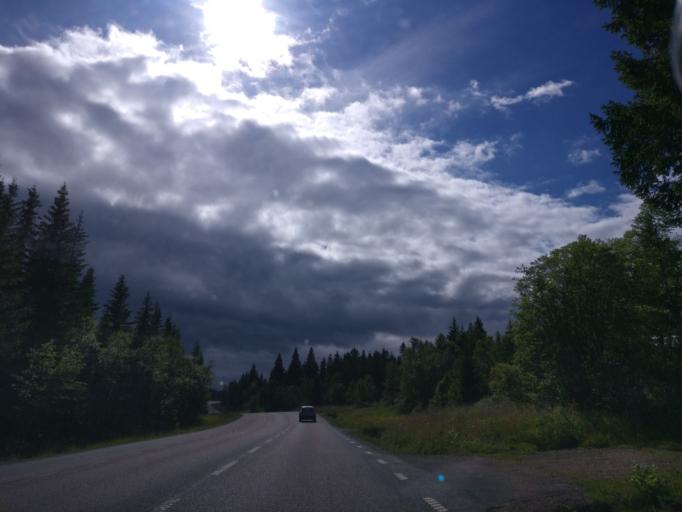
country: SE
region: Dalarna
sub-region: Malung-Saelens kommun
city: Malung
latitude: 61.1609
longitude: 13.1407
